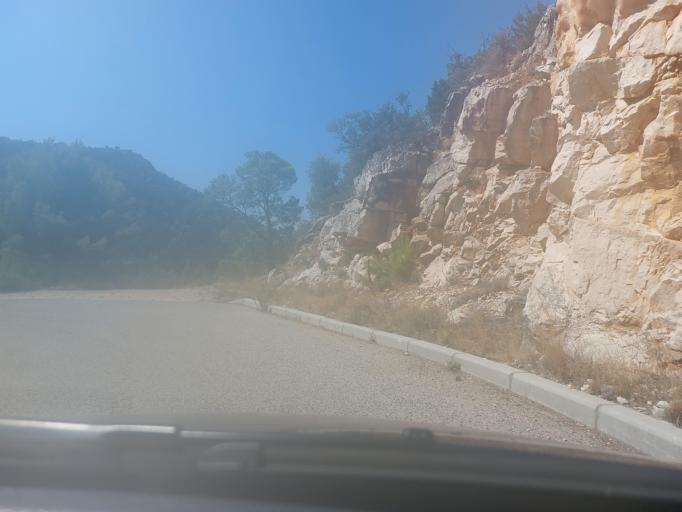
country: HR
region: Dubrovacko-Neretvanska
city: Smokvica
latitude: 42.7493
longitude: 16.8420
